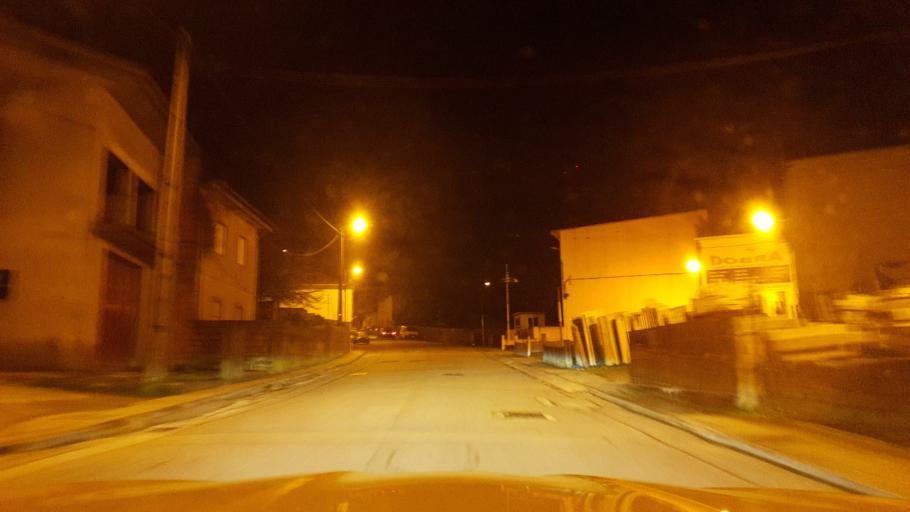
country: PT
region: Porto
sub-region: Matosinhos
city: Senhora da Hora
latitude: 41.2064
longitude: -8.6425
